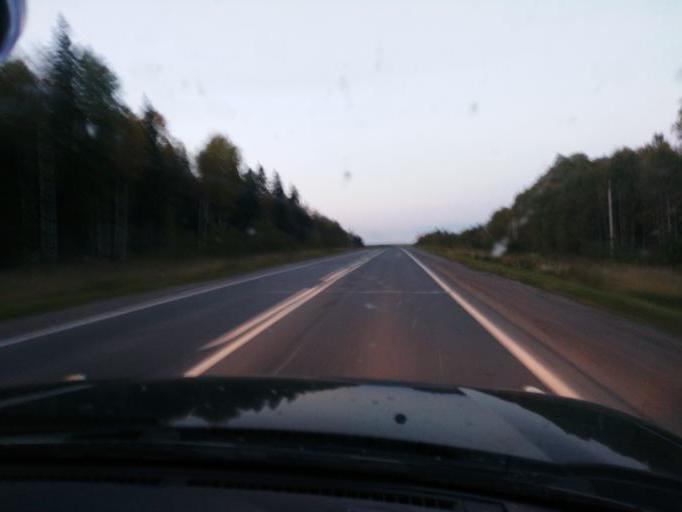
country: RU
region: Perm
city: Verkhnechusovskiye Gorodki
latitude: 58.2295
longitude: 57.2079
